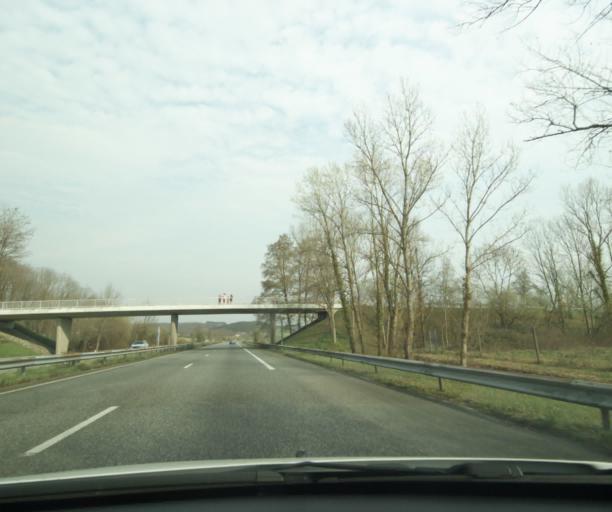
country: FR
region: Aquitaine
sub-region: Departement des Pyrenees-Atlantiques
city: Denguin
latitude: 43.3850
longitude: -0.5206
